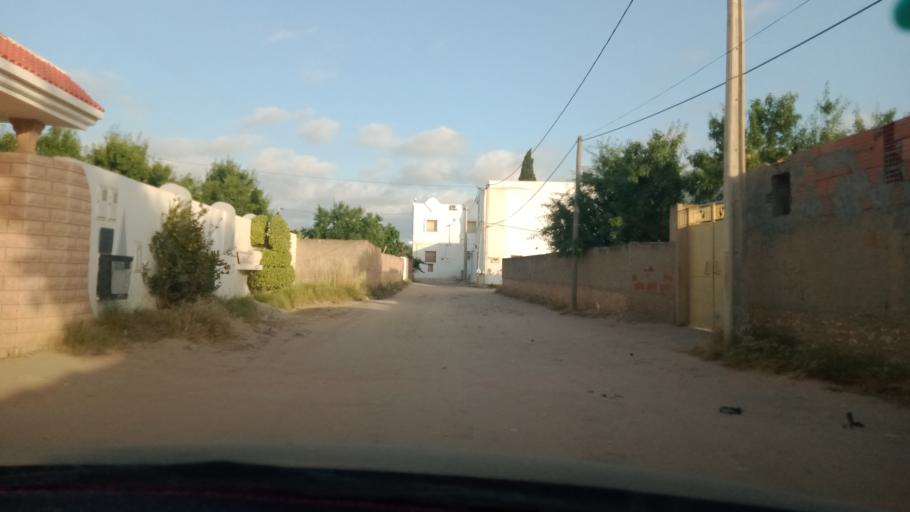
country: TN
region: Safaqis
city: Al Qarmadah
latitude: 34.8164
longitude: 10.7481
